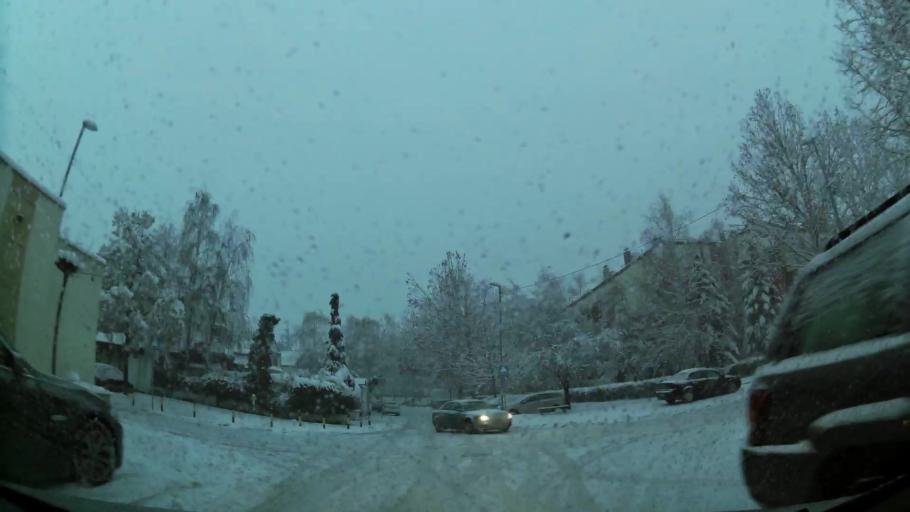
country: RS
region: Central Serbia
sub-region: Belgrade
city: Zemun
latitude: 44.8158
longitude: 20.3858
